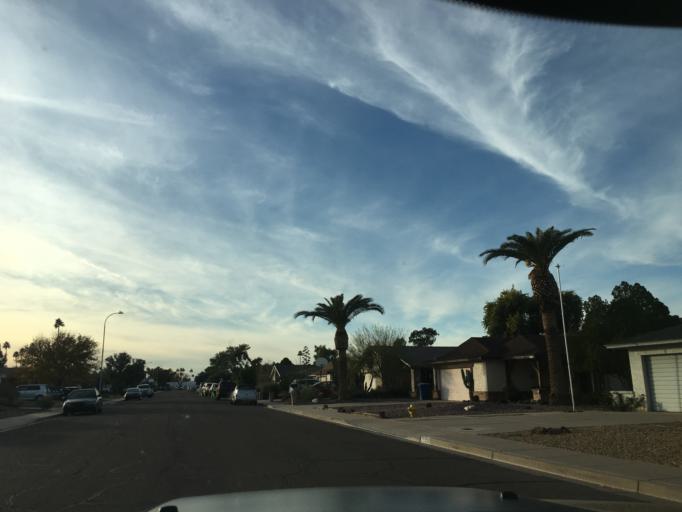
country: US
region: Arizona
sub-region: Maricopa County
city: Tempe
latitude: 33.3765
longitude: -111.9061
